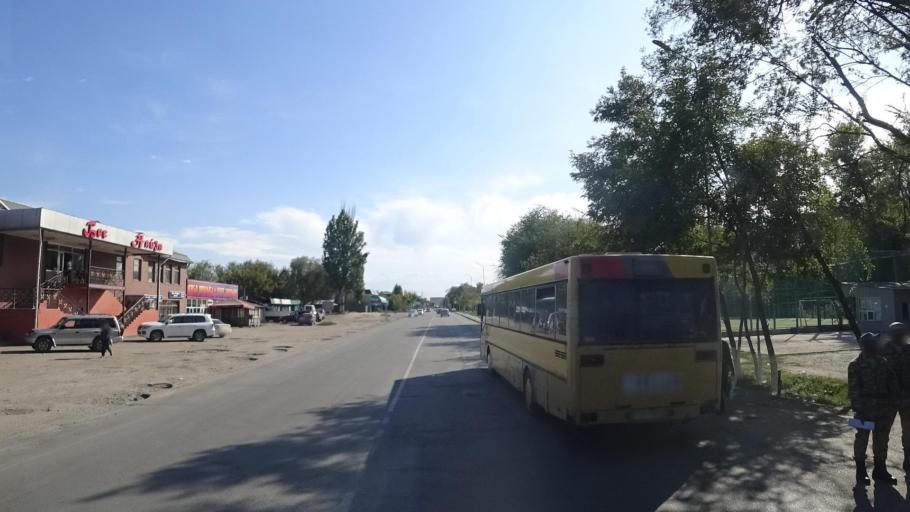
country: KZ
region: Almaty Oblysy
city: Energeticheskiy
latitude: 43.4162
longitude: 77.0210
